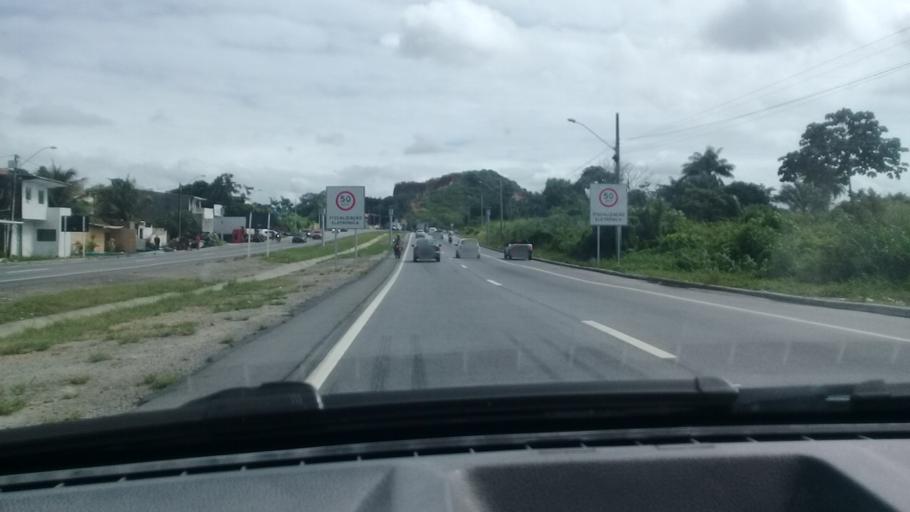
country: BR
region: Pernambuco
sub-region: Jaboatao Dos Guararapes
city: Jaboatao dos Guararapes
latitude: -8.1083
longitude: -34.9478
